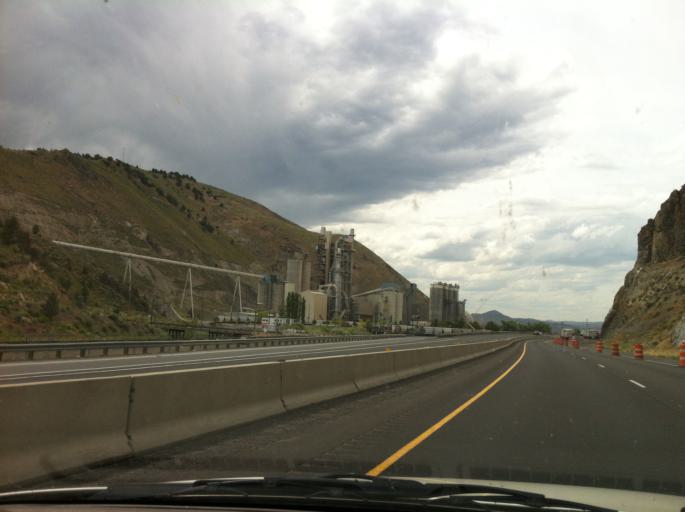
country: US
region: Oregon
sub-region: Baker County
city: Baker City
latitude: 44.5391
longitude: -117.4147
